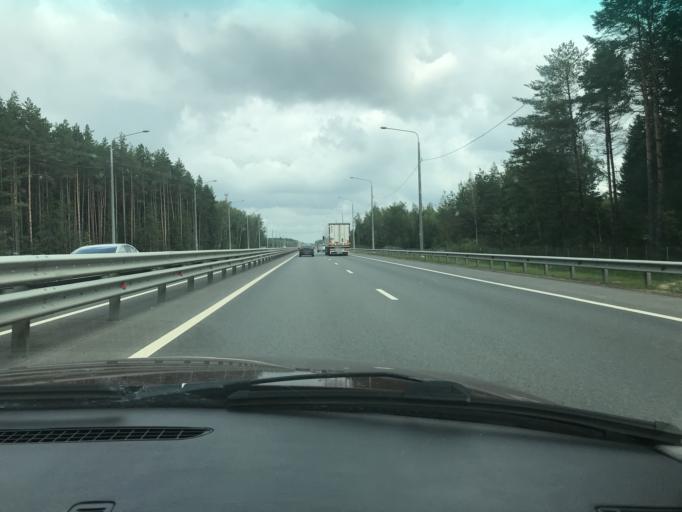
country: RU
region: Kaluga
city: Pyatovskiy
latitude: 54.7041
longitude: 36.1606
